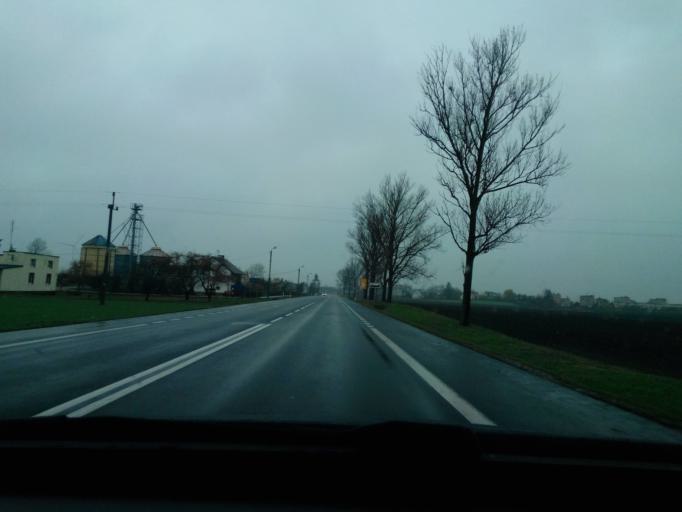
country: PL
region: Pomeranian Voivodeship
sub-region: Powiat tczewski
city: Gniew
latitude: 53.9002
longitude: 18.7868
